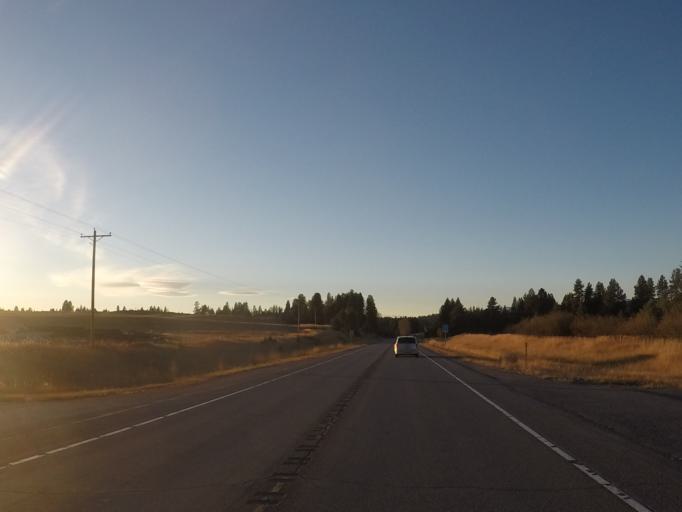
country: US
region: Montana
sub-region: Lewis and Clark County
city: Lincoln
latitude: 46.9969
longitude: -113.0290
